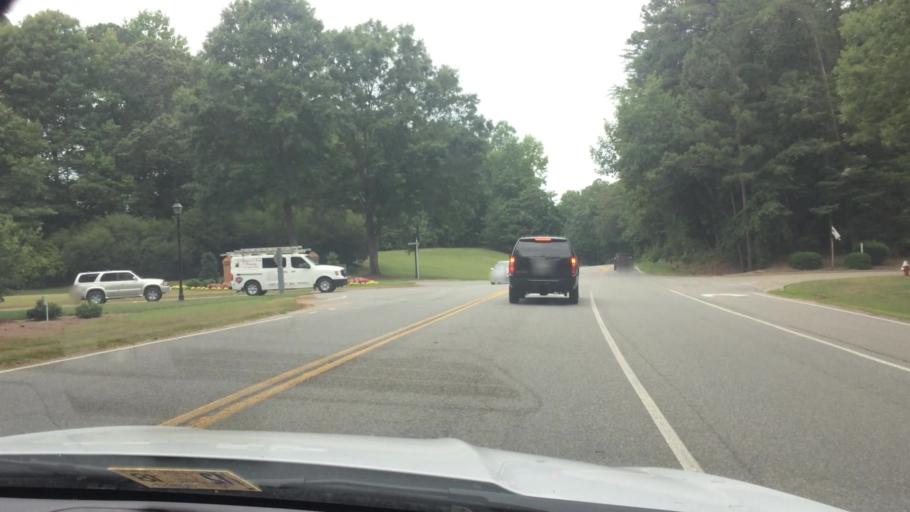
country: US
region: Virginia
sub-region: James City County
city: Williamsburg
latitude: 37.3134
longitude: -76.7757
